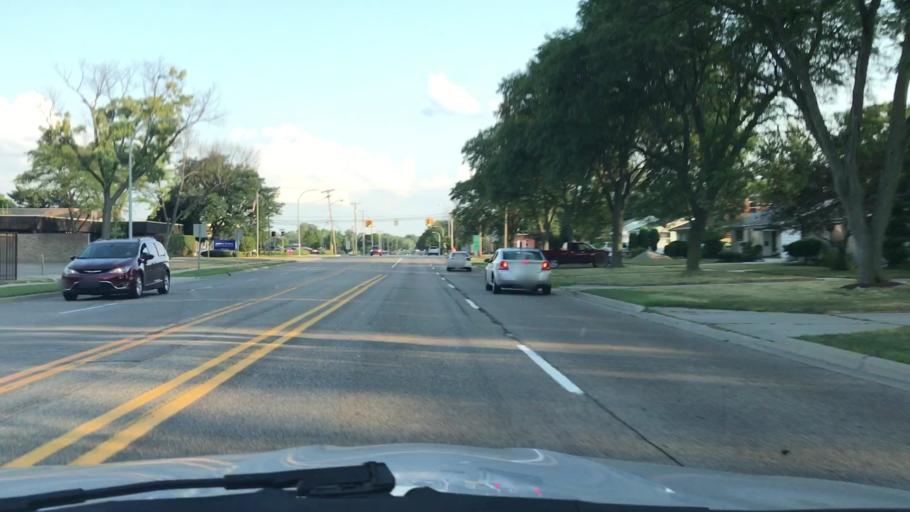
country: US
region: Michigan
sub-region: Oakland County
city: Clawson
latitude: 42.5267
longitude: -83.1653
